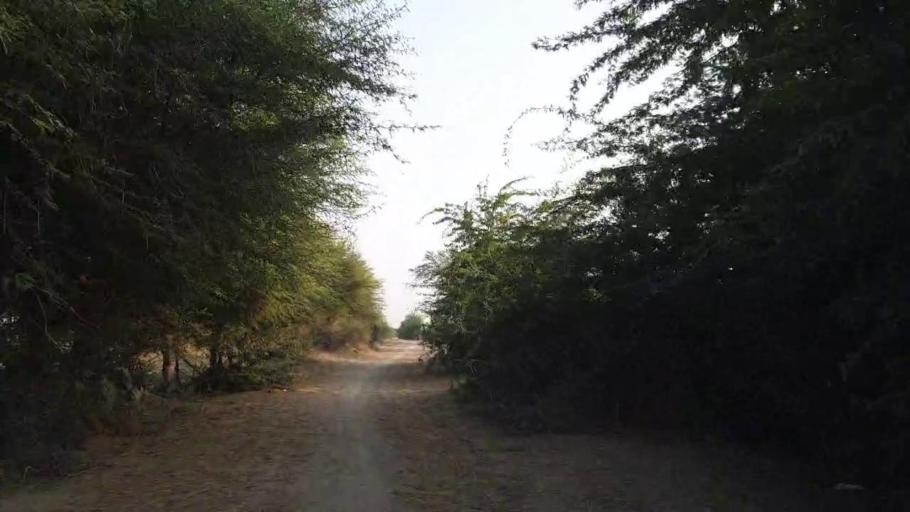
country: PK
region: Sindh
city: Kario
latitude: 24.8628
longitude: 68.6238
